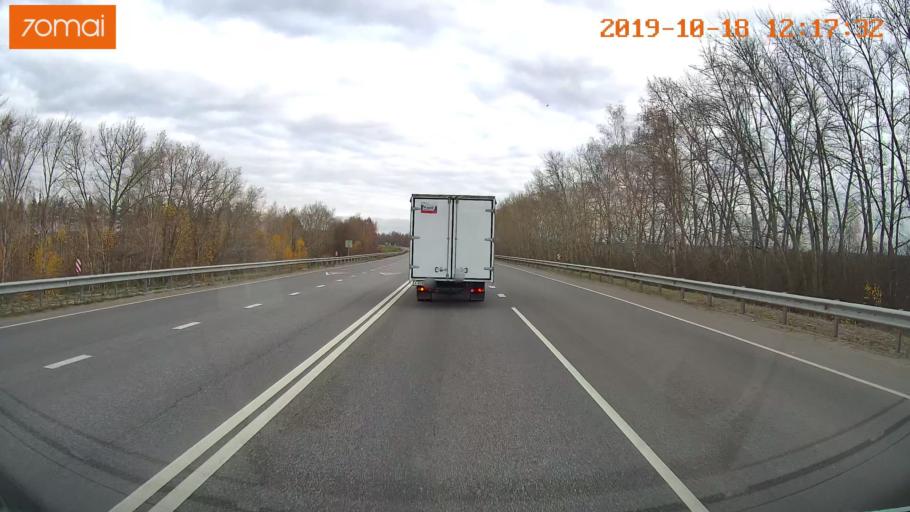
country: RU
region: Rjazan
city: Zakharovo
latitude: 54.4582
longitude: 39.4448
